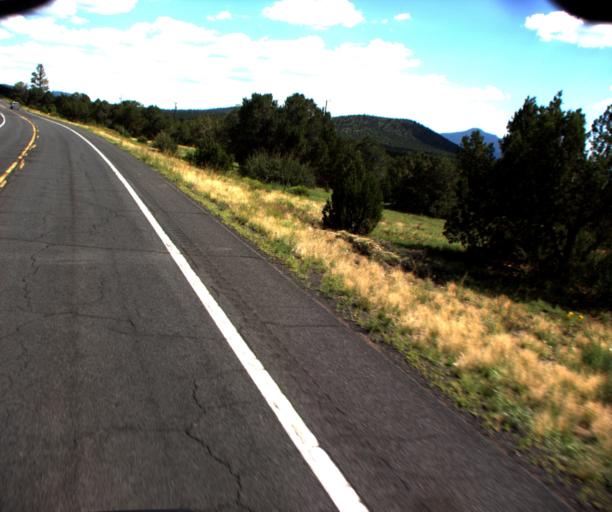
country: US
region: Arizona
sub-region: Coconino County
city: Williams
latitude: 35.3439
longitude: -112.1659
